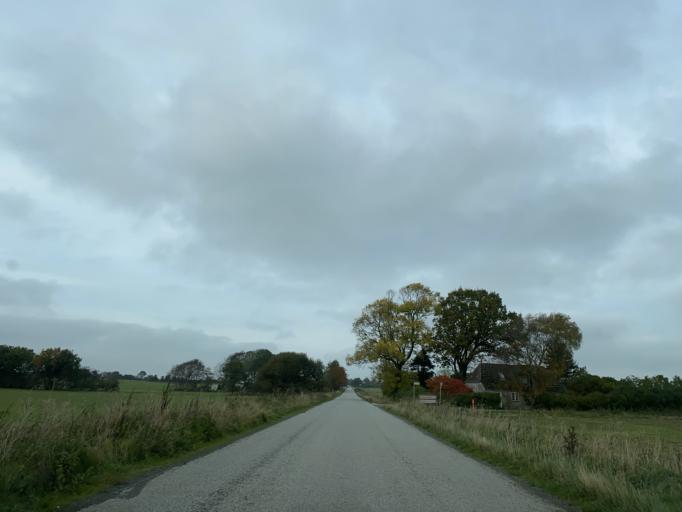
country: DK
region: South Denmark
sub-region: Haderslev Kommune
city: Starup
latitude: 55.1808
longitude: 9.5171
